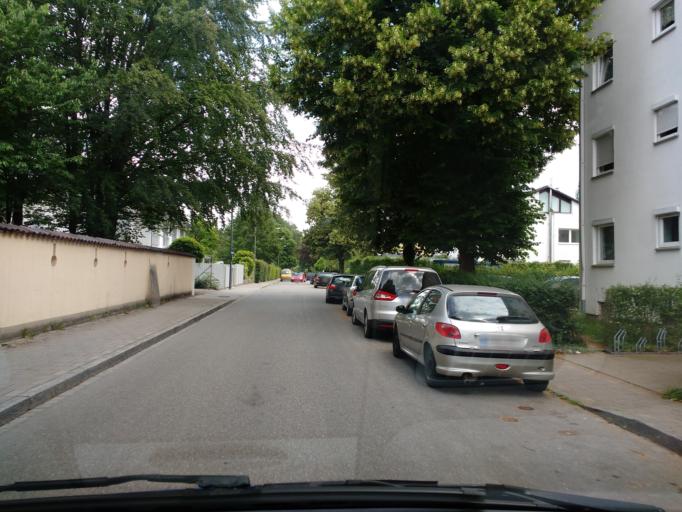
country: DE
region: Bavaria
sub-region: Upper Bavaria
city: Rosenheim
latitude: 47.8669
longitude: 12.1134
